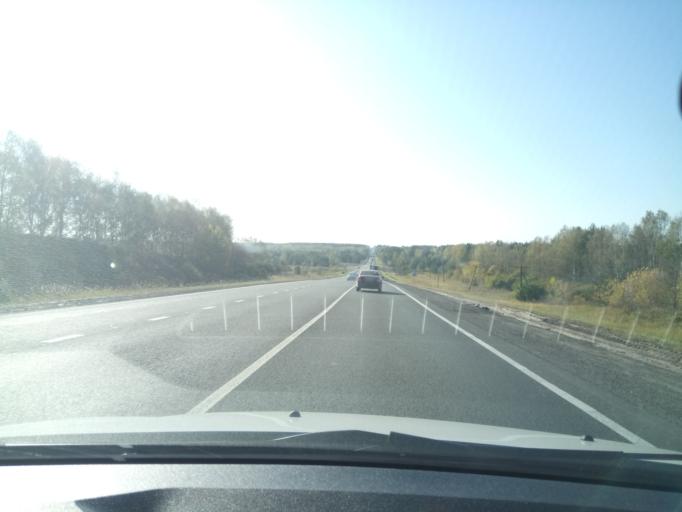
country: RU
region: Nizjnij Novgorod
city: Dal'neye Konstantinovo
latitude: 55.9638
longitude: 43.9751
